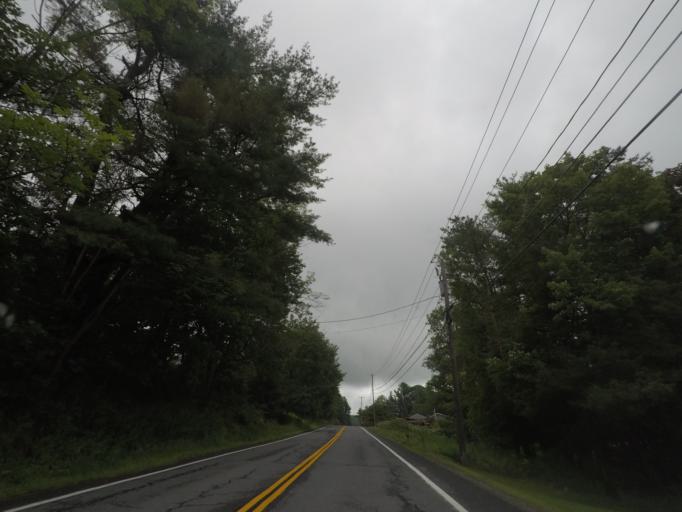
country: US
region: New York
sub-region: Rensselaer County
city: Averill Park
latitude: 42.5887
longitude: -73.4925
